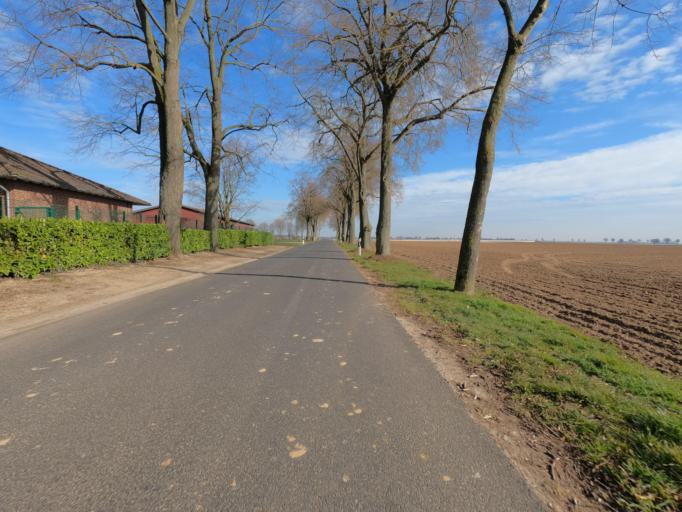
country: DE
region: North Rhine-Westphalia
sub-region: Regierungsbezirk Koln
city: Linnich
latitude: 51.0130
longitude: 6.3225
